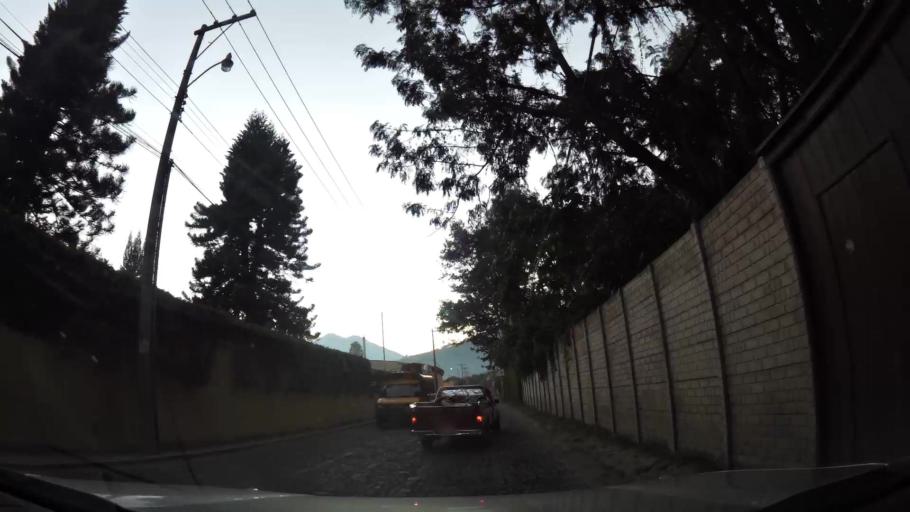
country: GT
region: Sacatepequez
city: Antigua Guatemala
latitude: 14.5522
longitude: -90.7385
